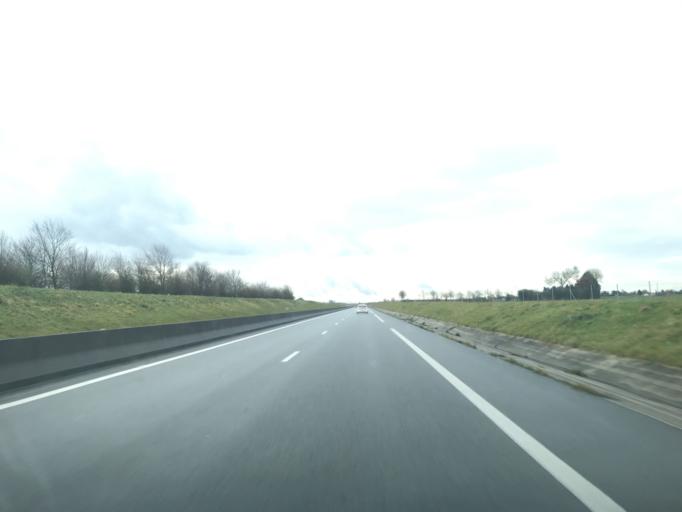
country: FR
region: Haute-Normandie
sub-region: Departement de l'Eure
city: Thiberville
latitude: 49.0714
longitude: 0.4718
